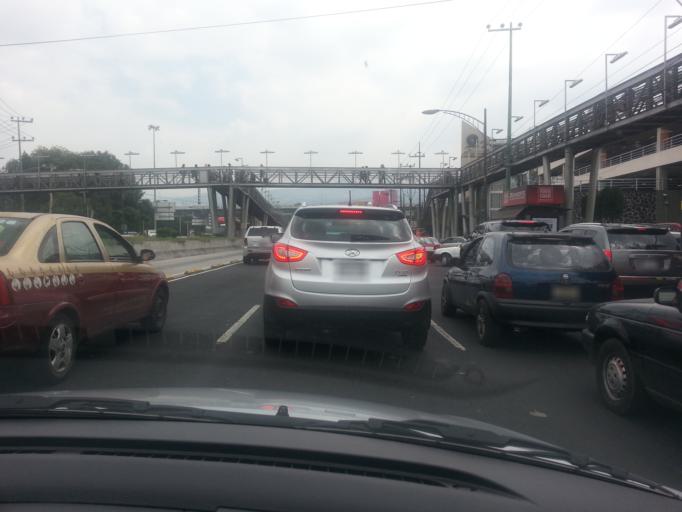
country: MX
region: Mexico City
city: Tlalpan
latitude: 19.3057
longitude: -99.1864
